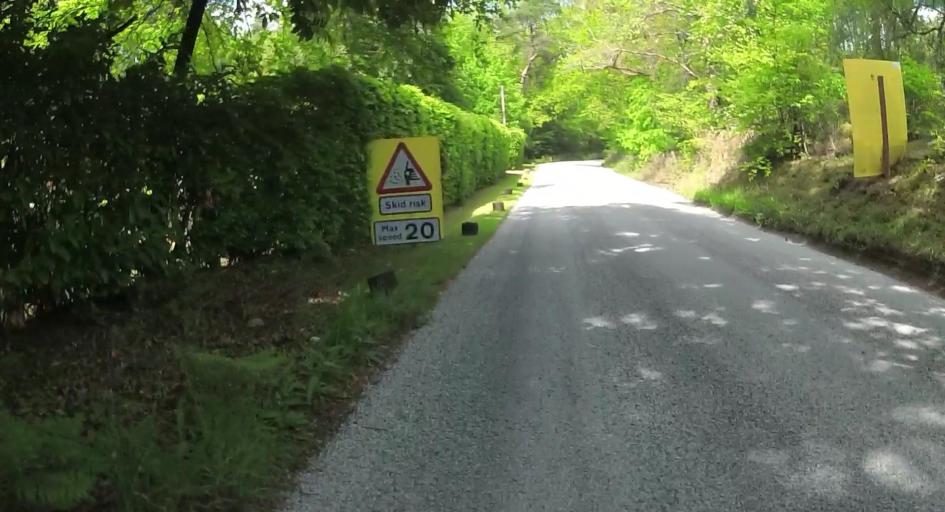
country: GB
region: England
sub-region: Surrey
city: Farnham
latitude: 51.1859
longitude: -0.7992
